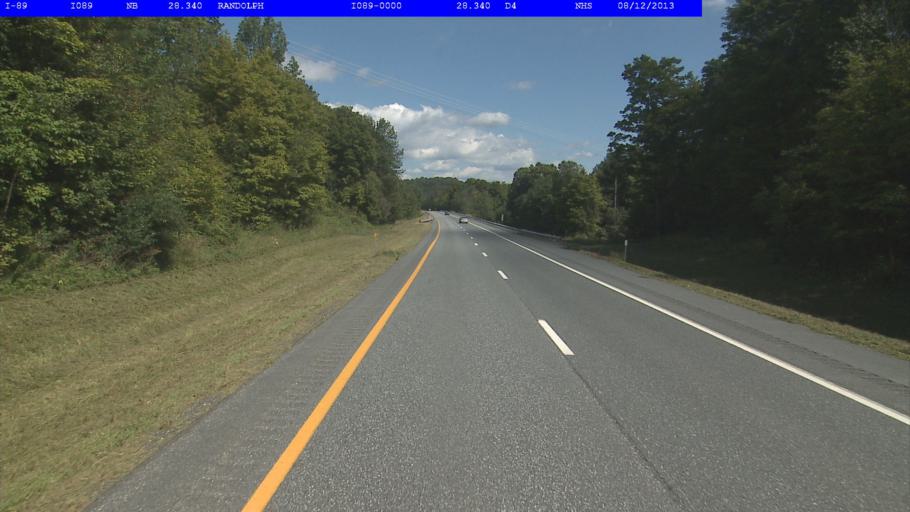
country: US
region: Vermont
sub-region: Orange County
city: Randolph
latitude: 43.9084
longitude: -72.6130
